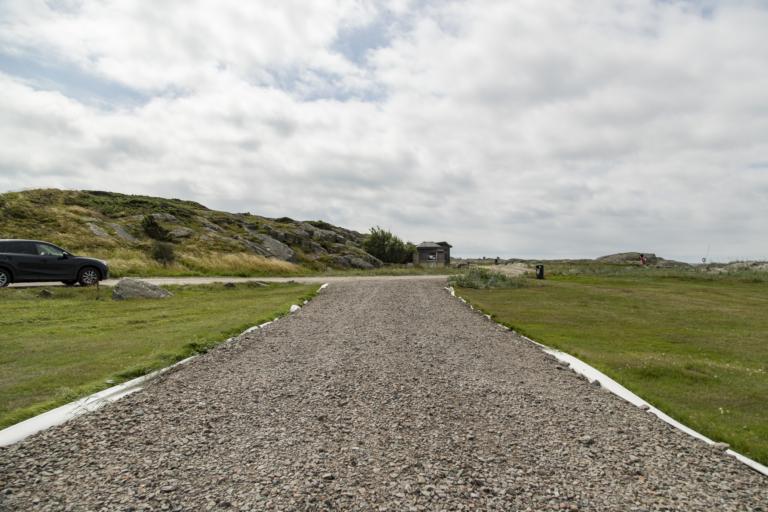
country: SE
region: Halland
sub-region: Varbergs Kommun
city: Varberg
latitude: 57.1130
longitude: 12.2254
